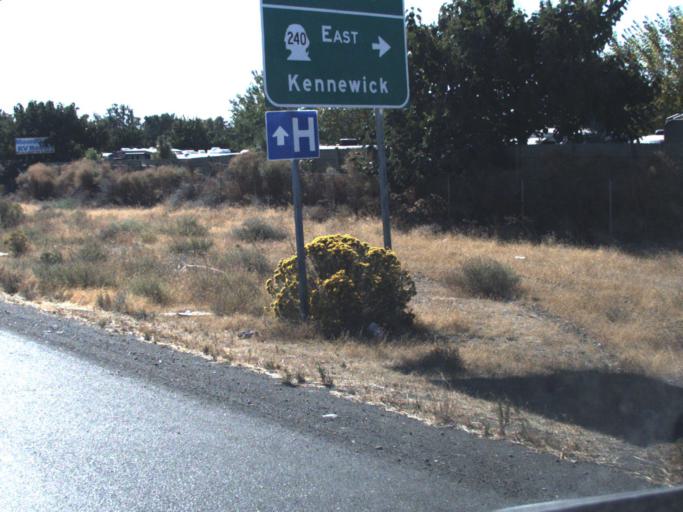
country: US
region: Washington
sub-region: Benton County
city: Richland
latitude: 46.3112
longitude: -119.2881
